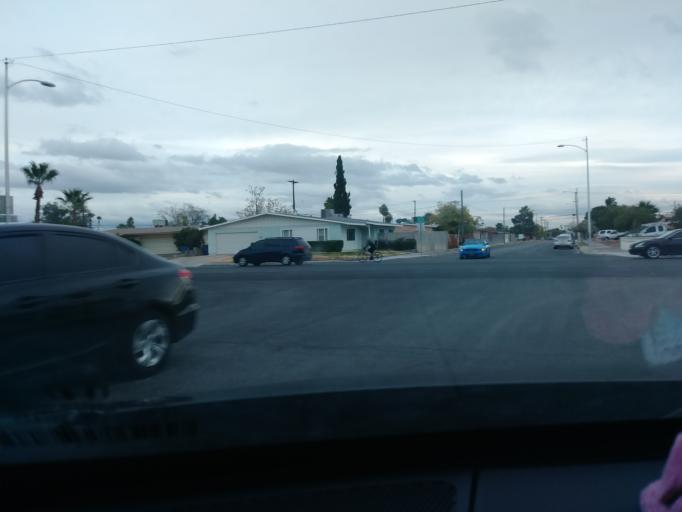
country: US
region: Nevada
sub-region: Clark County
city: Spring Valley
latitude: 36.1666
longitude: -115.2228
